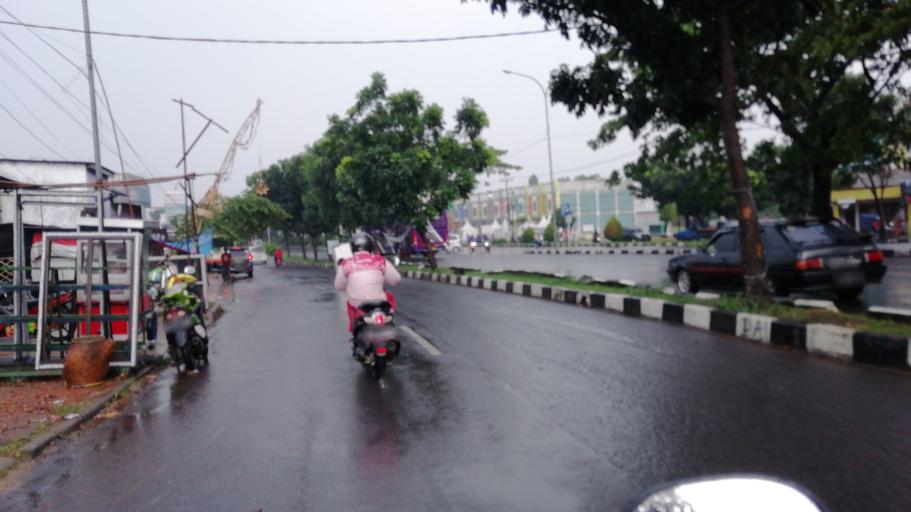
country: ID
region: West Java
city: Cibinong
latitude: -6.4816
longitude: 106.8093
